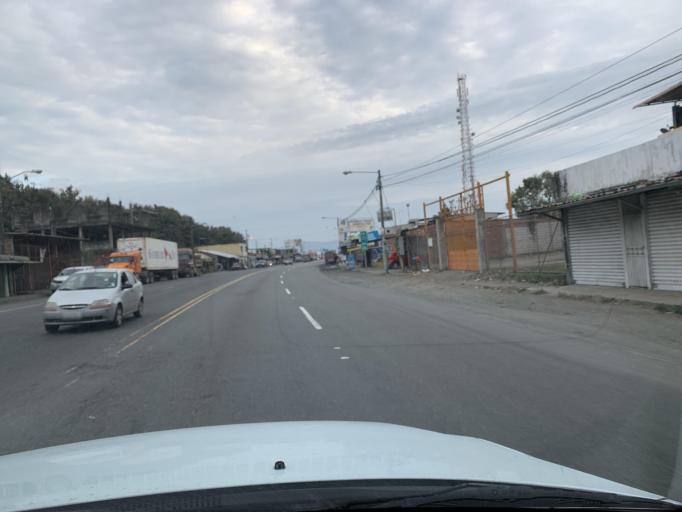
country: EC
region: Guayas
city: Yaguachi Nuevo
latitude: -2.2483
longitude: -79.6354
